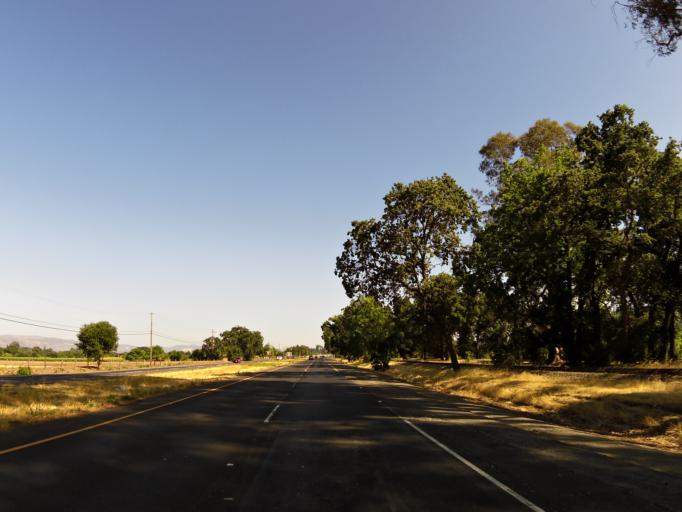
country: US
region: California
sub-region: Napa County
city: Yountville
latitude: 38.3907
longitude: -122.3528
